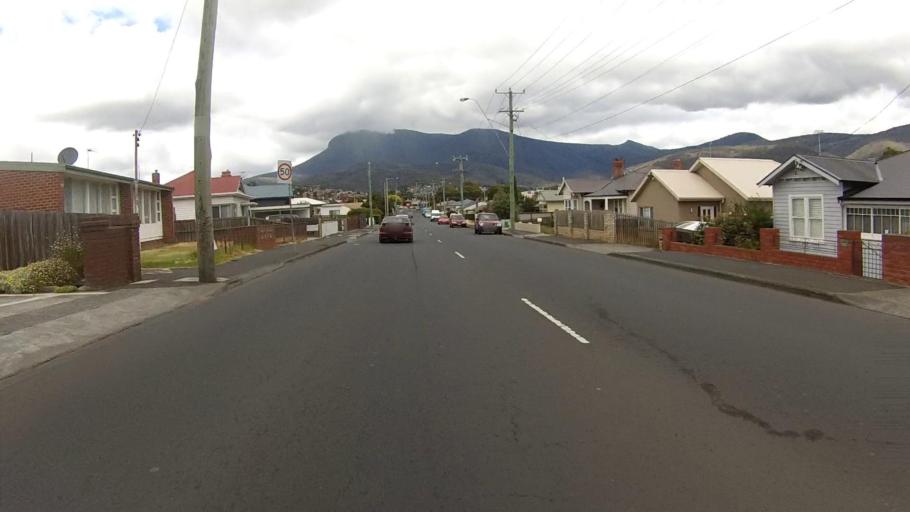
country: AU
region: Tasmania
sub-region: Glenorchy
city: Glenorchy
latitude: -42.8303
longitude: 147.2820
